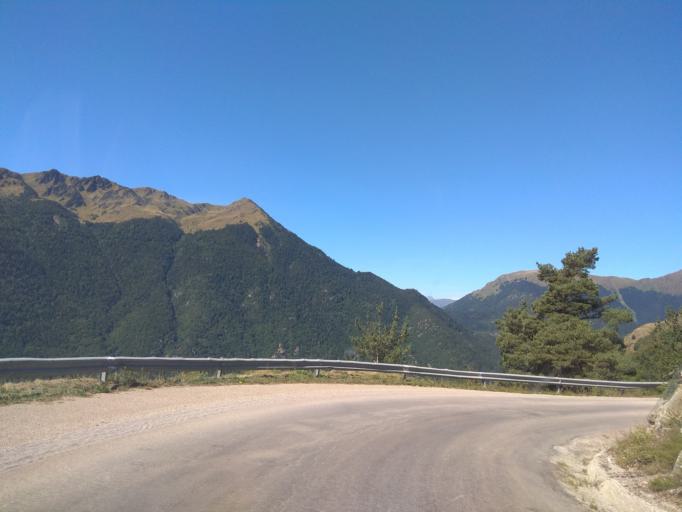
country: ES
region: Catalonia
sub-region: Provincia de Lleida
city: Les
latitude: 42.7501
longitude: 0.7167
